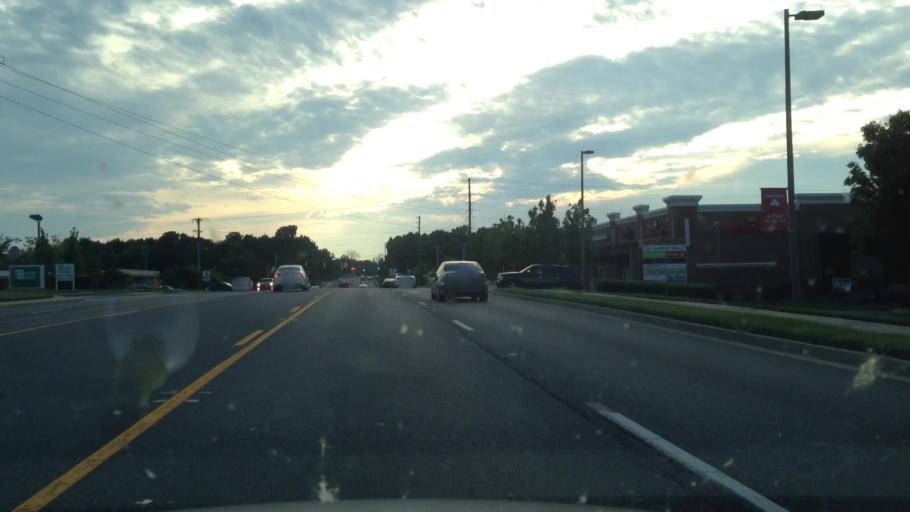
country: US
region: South Carolina
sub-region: York County
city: Fort Mill
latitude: 35.0613
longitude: -80.9616
